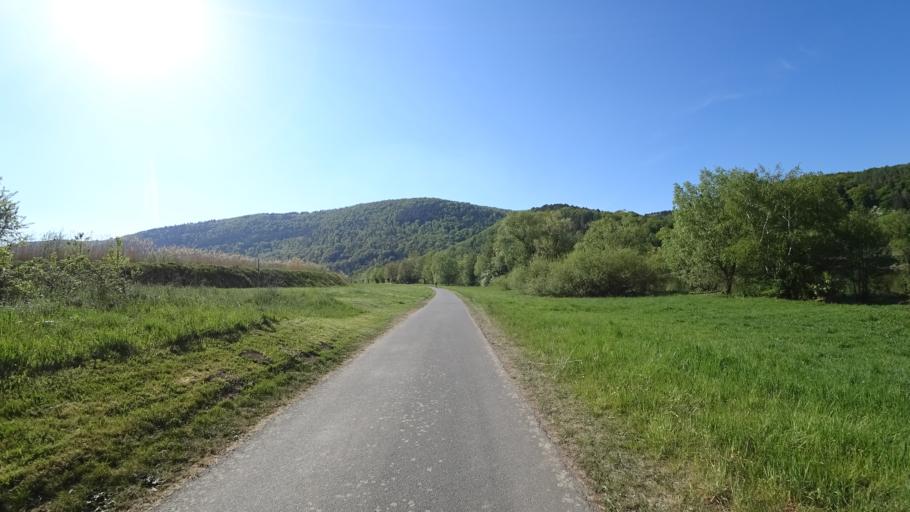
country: DE
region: Bavaria
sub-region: Regierungsbezirk Unterfranken
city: Burgstadt
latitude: 49.7403
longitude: 9.2904
